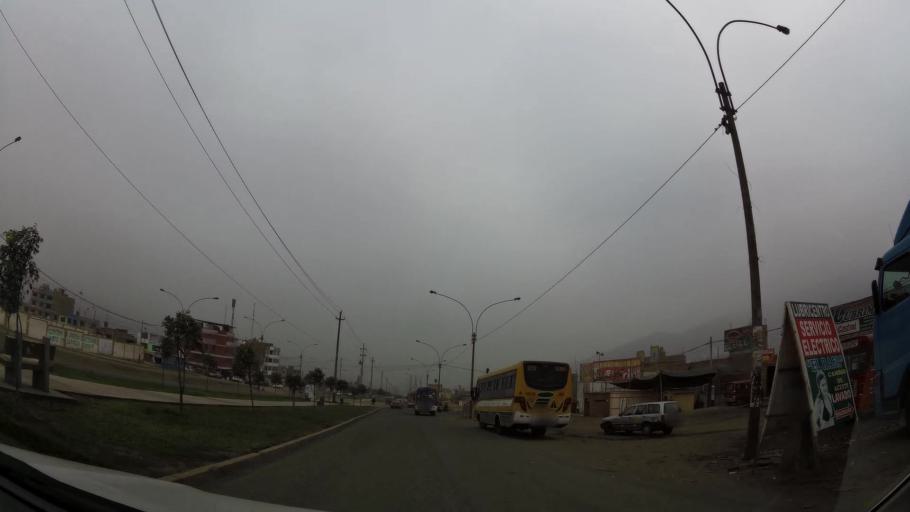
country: PE
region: Lima
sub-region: Lima
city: Urb. Santo Domingo
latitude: -11.9229
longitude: -76.9621
